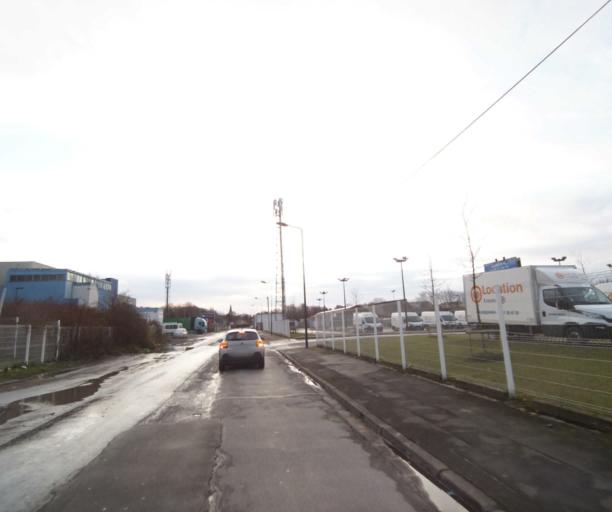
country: FR
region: Nord-Pas-de-Calais
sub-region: Departement du Nord
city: Saint-Saulve
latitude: 50.3747
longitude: 3.5409
